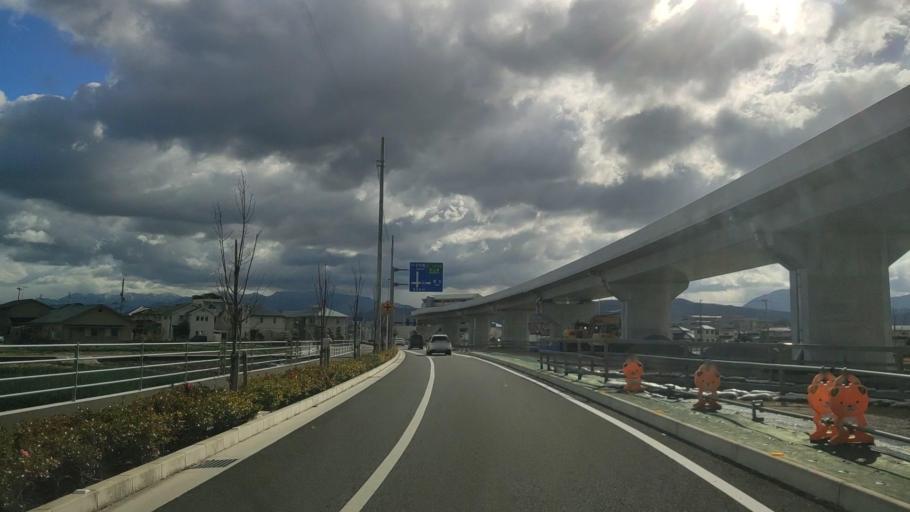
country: JP
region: Ehime
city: Masaki-cho
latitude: 33.8131
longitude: 132.7221
